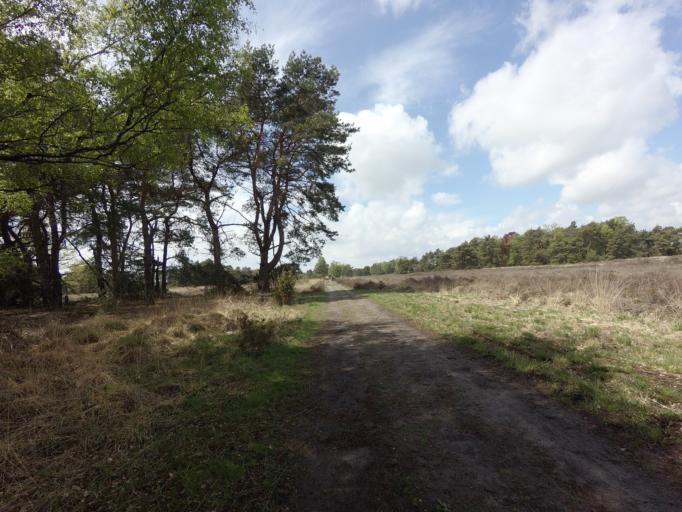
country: NL
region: Overijssel
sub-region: Gemeente Haaksbergen
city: Haaksbergen
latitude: 52.1587
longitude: 6.7917
